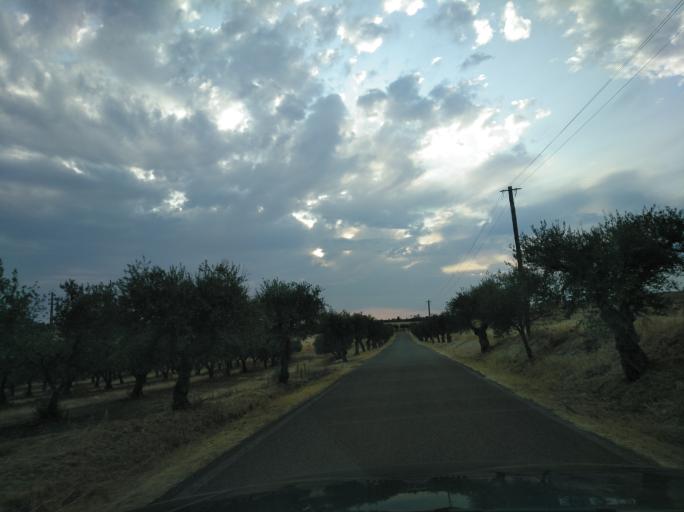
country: PT
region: Portalegre
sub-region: Campo Maior
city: Campo Maior
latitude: 39.0159
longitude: -7.0342
